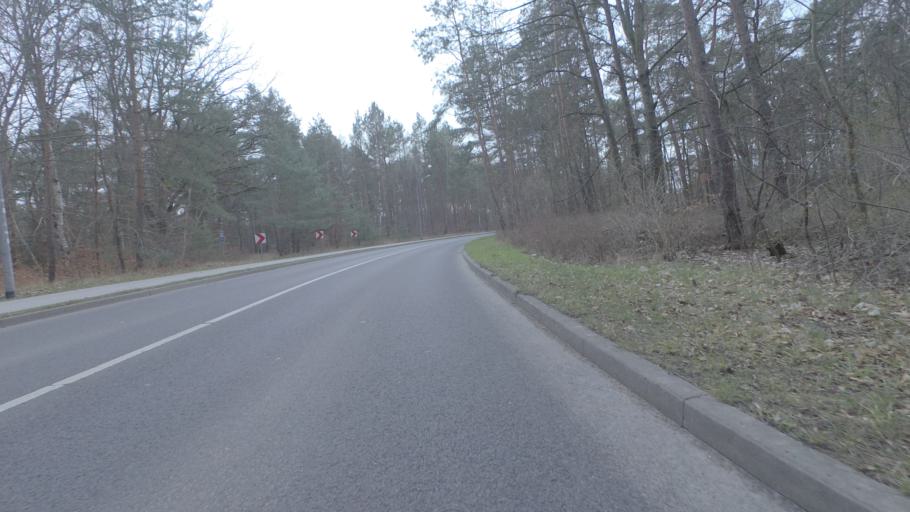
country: DE
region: Brandenburg
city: Ludwigsfelde
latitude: 52.3121
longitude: 13.2629
